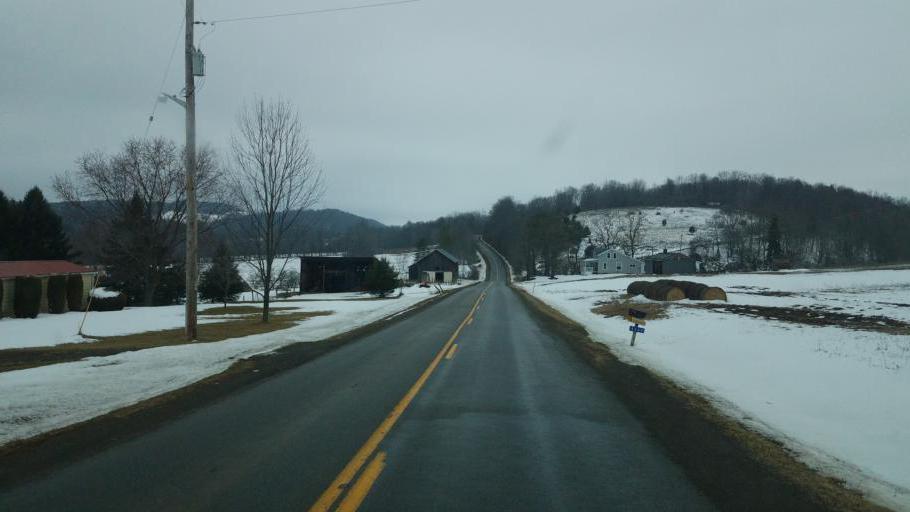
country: US
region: Pennsylvania
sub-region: Tioga County
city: Westfield
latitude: 42.0800
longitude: -77.4690
